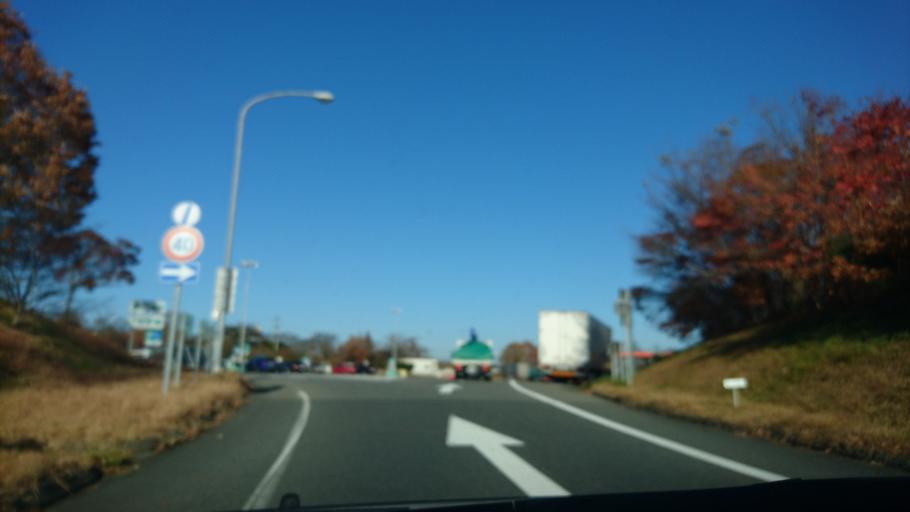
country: JP
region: Miyagi
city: Furukawa
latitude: 38.6367
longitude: 140.9591
